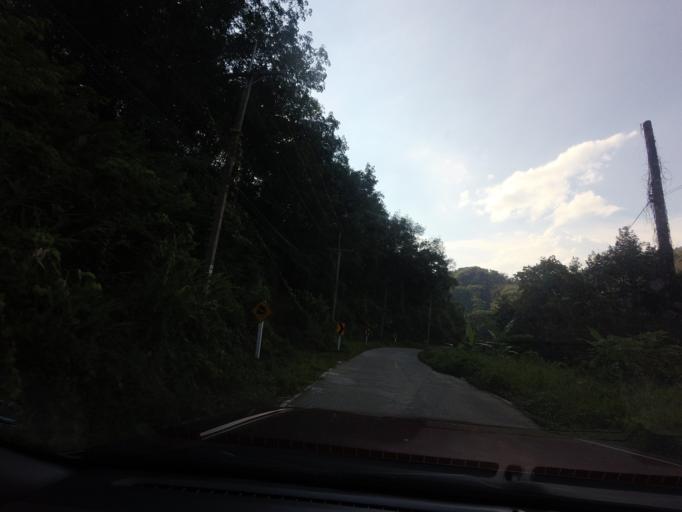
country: TH
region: Yala
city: Than To
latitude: 6.0934
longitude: 101.3149
